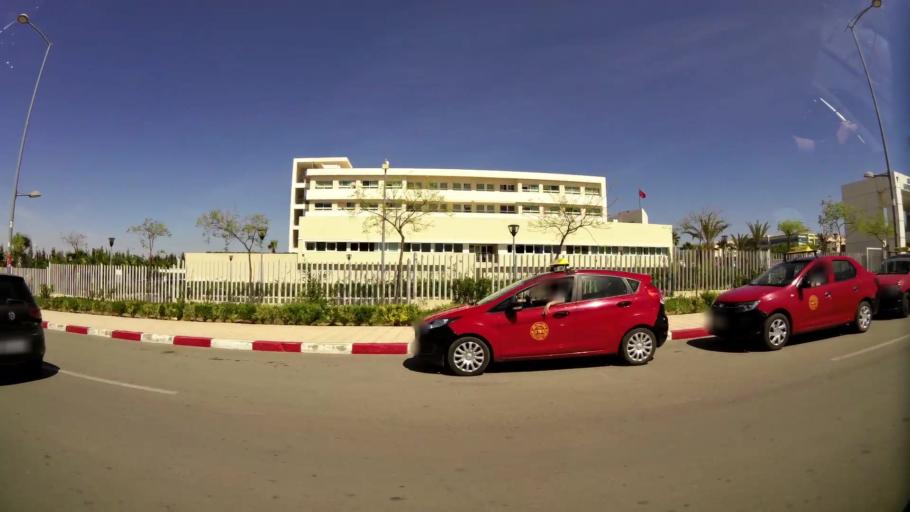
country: MA
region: Oriental
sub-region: Oujda-Angad
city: Oujda
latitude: 34.6567
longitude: -1.9127
